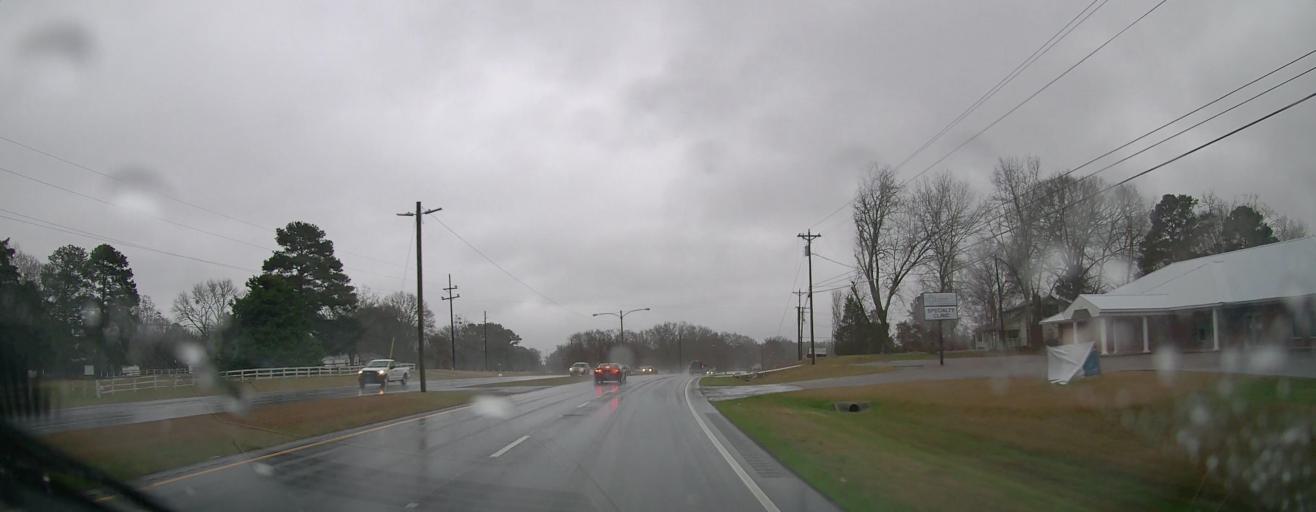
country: US
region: Alabama
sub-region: Morgan County
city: Hartselle
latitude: 34.4608
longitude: -86.9483
